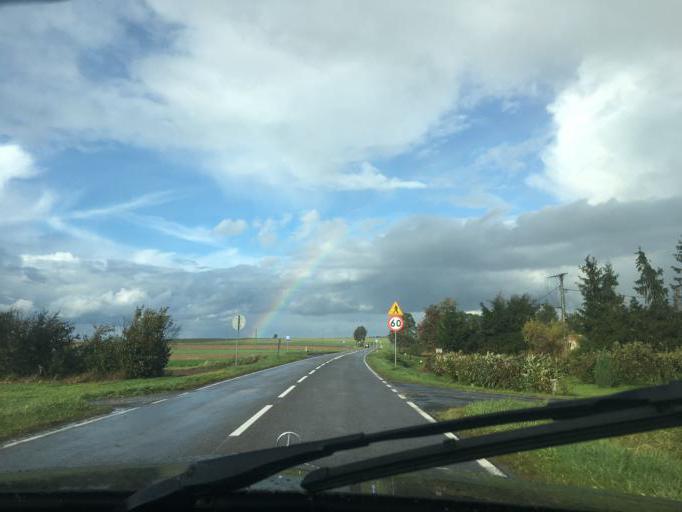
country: PL
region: Lublin Voivodeship
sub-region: Powiat swidnicki
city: Piaski
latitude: 51.1096
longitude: 22.7474
